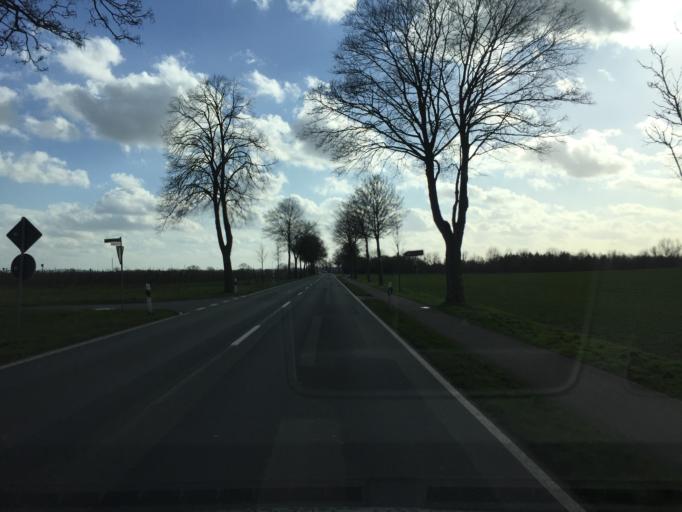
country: DE
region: Lower Saxony
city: Stolzenau
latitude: 52.5340
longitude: 9.0749
